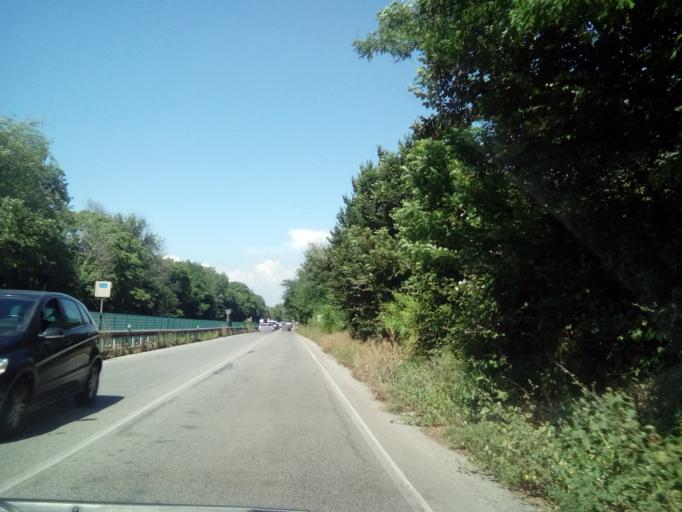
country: VA
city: Vatican City
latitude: 41.8359
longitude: 12.4578
